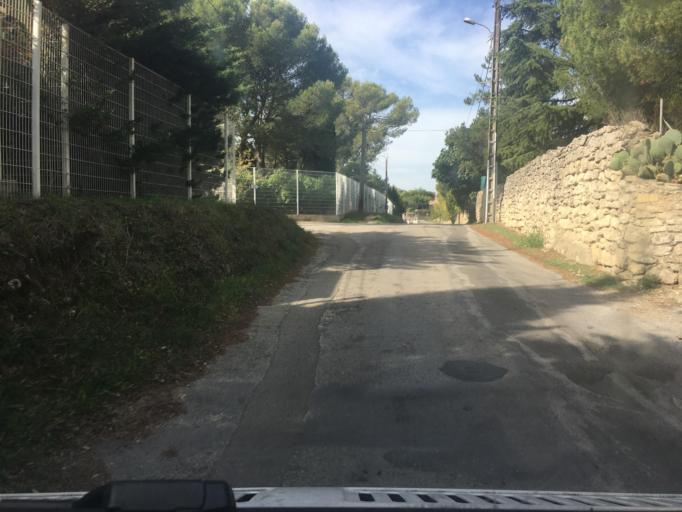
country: FR
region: Languedoc-Roussillon
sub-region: Departement du Gard
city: Uzes
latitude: 44.0081
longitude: 4.4120
